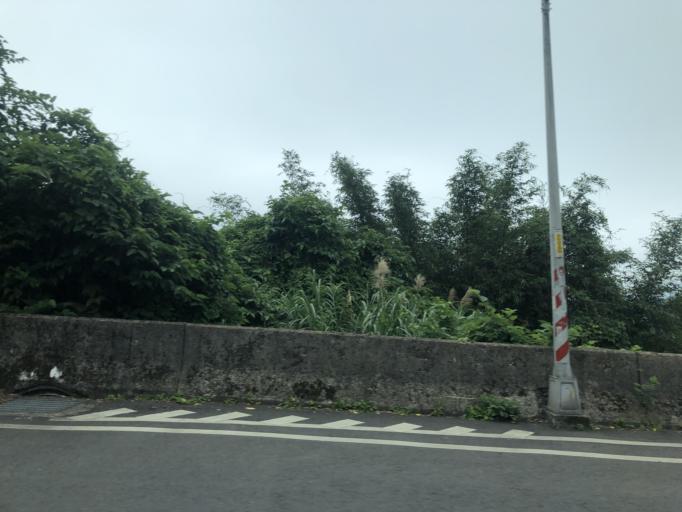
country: TW
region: Taiwan
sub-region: Keelung
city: Keelung
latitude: 25.1923
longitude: 121.6801
